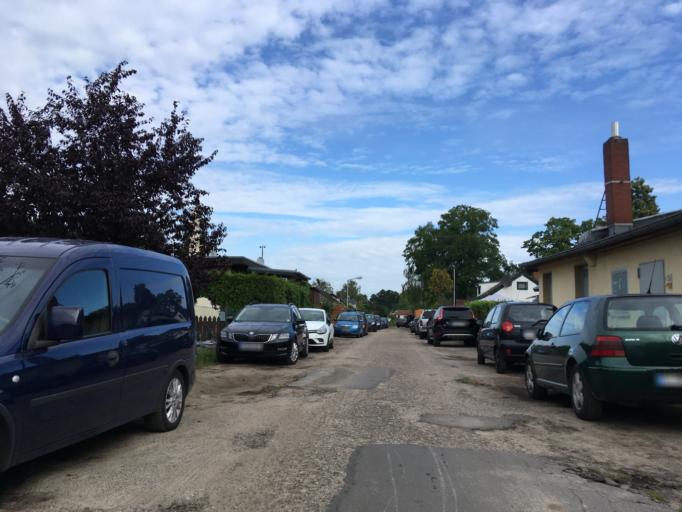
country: DE
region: Berlin
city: Konradshohe
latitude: 52.5694
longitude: 13.2217
